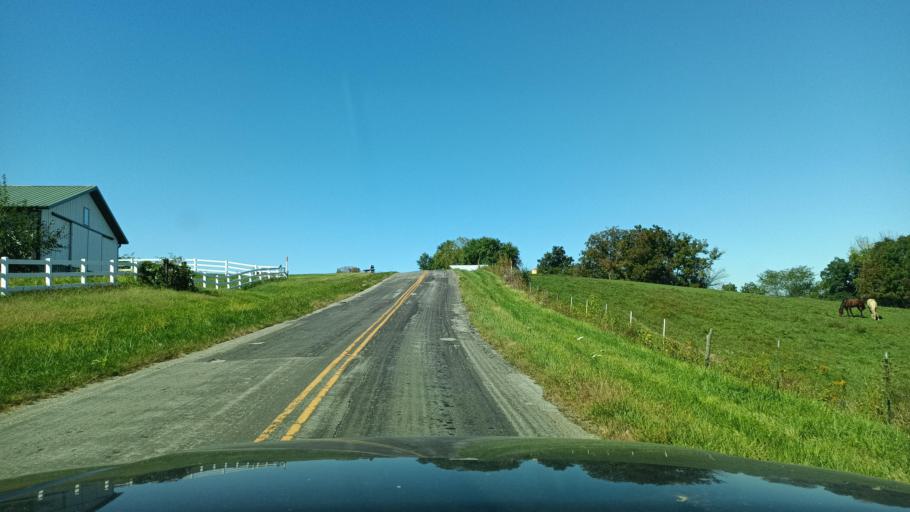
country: US
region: Missouri
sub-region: Scotland County
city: Memphis
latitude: 40.3549
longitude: -92.2518
